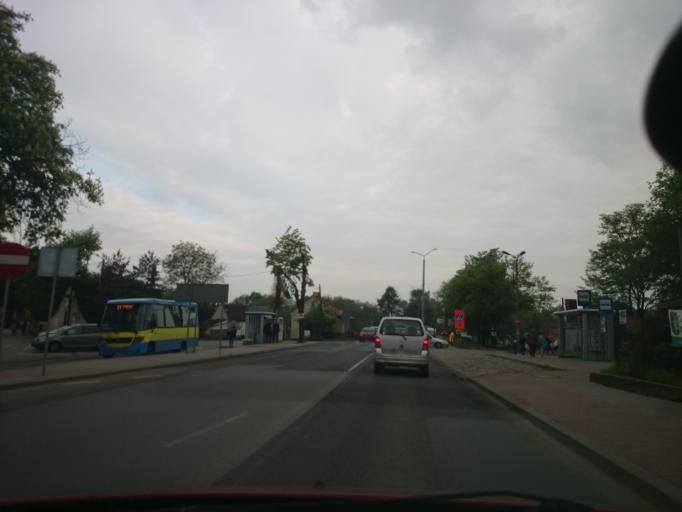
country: PL
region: Opole Voivodeship
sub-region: Powiat opolski
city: Czarnowasy
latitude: 50.7204
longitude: 17.9023
